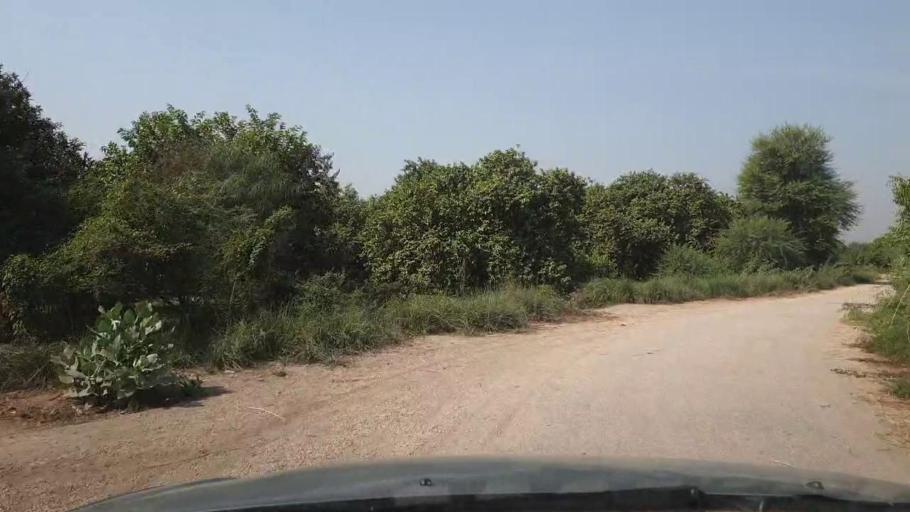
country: PK
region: Sindh
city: Tando Jam
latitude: 25.3639
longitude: 68.5270
